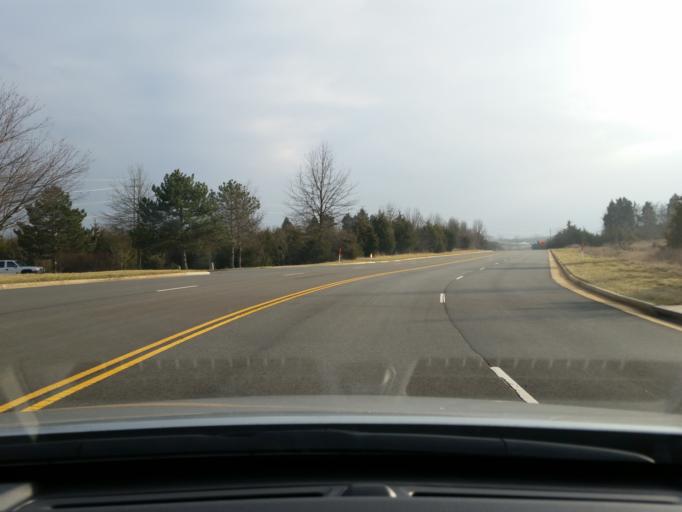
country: US
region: Virginia
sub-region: Loudoun County
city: Sterling
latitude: 39.0138
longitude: -77.4527
